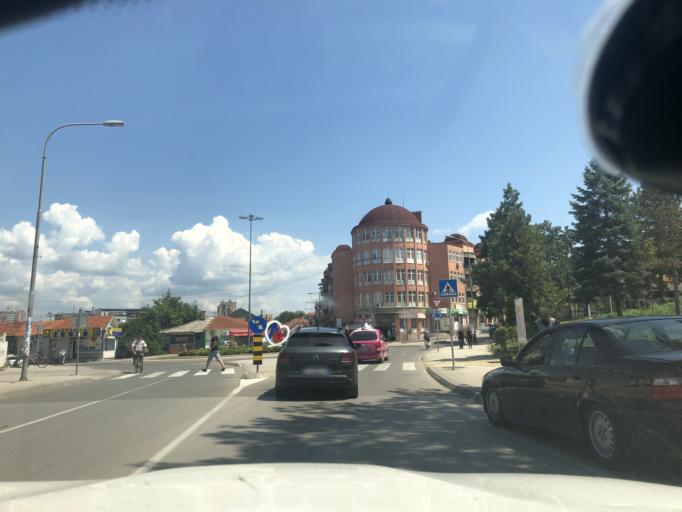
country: RS
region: Central Serbia
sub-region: Jablanicki Okrug
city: Leskovac
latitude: 42.9943
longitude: 21.9378
